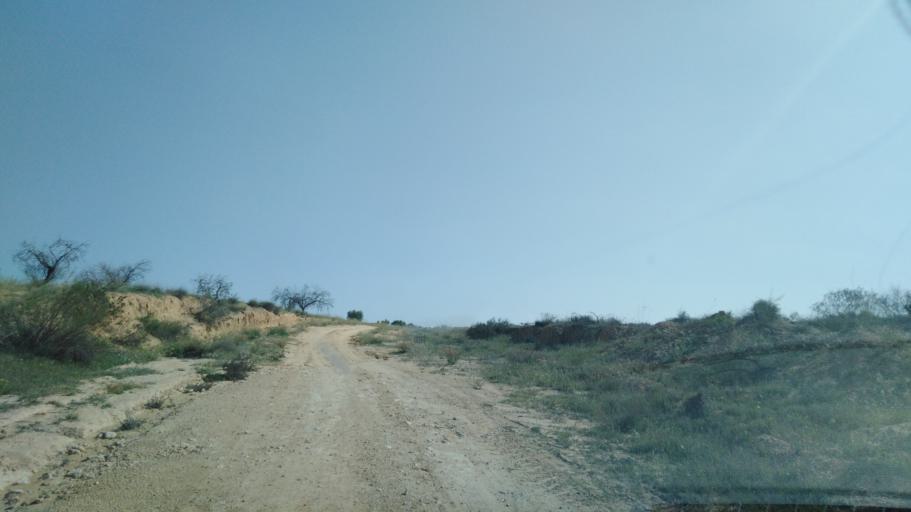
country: TN
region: Safaqis
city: Bi'r `Ali Bin Khalifah
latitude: 34.7875
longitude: 10.3699
